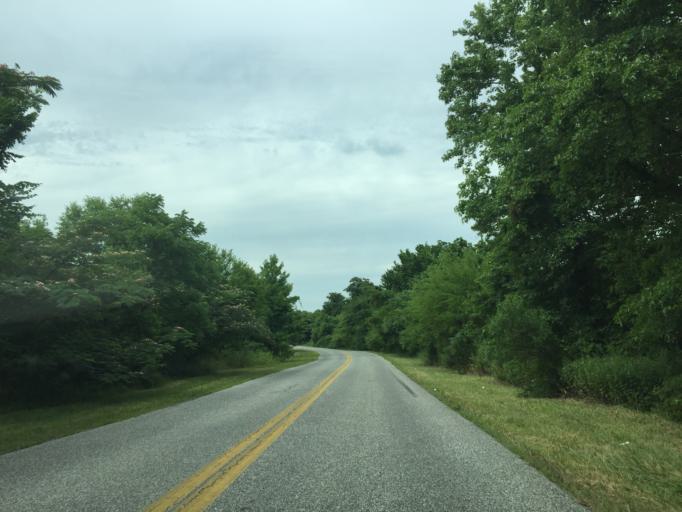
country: US
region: Maryland
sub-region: Baltimore County
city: Edgemere
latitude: 39.2593
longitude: -76.4554
